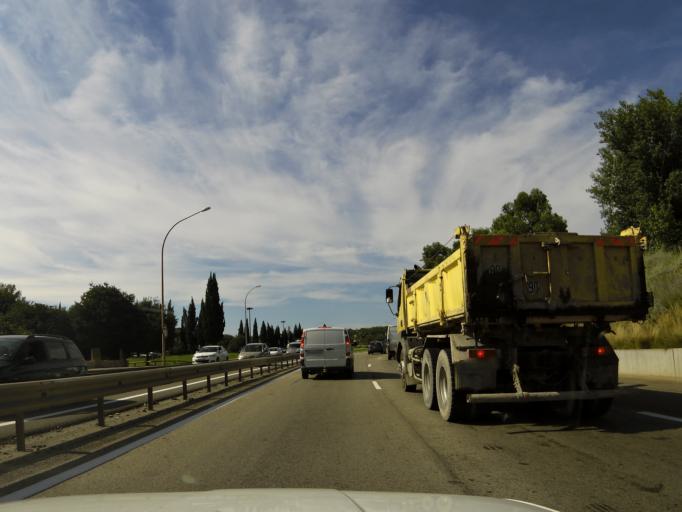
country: FR
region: Languedoc-Roussillon
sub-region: Departement du Gard
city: Nimes
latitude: 43.8223
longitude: 4.3289
